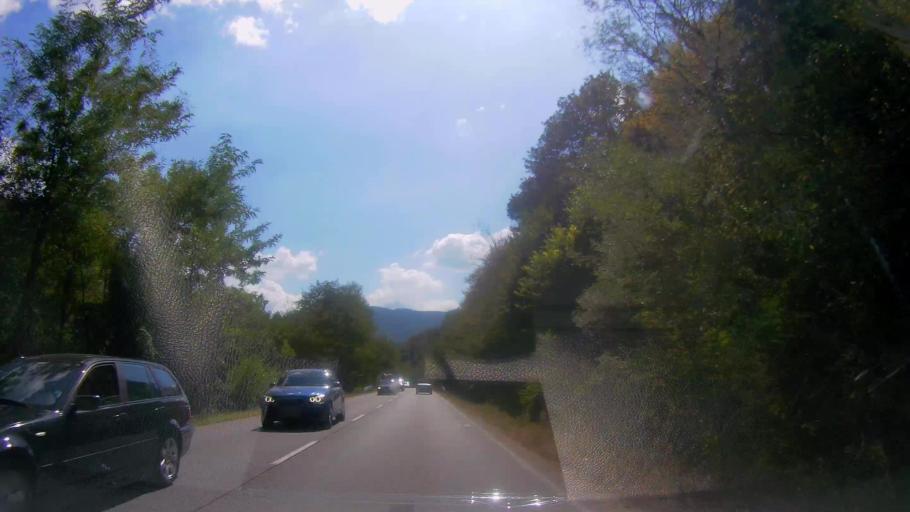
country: BG
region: Stara Zagora
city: Gurkovo
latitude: 42.7292
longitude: 25.7122
